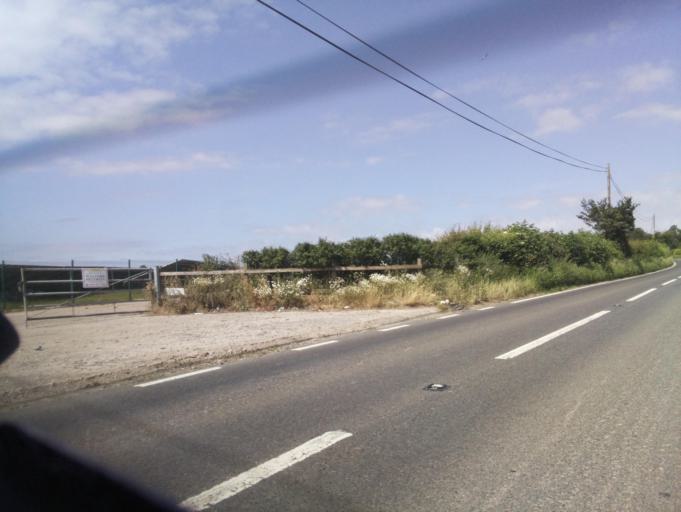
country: GB
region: England
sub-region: Somerset
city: Wincanton
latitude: 51.0565
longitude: -2.4502
